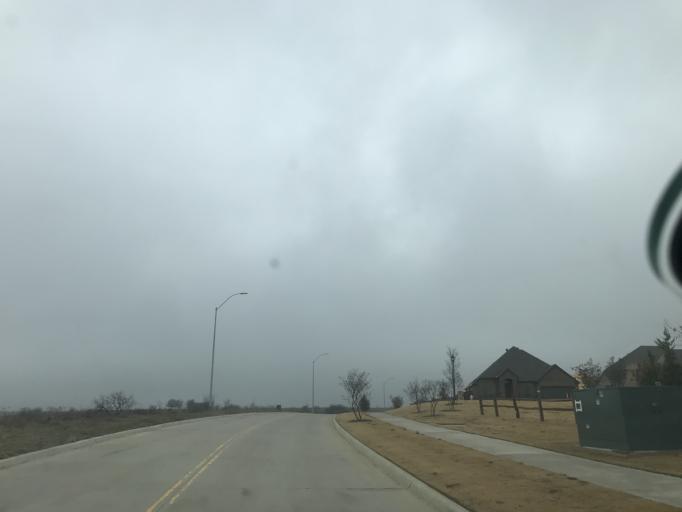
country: US
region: Texas
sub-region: Tarrant County
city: Crowley
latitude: 32.6125
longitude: -97.4167
